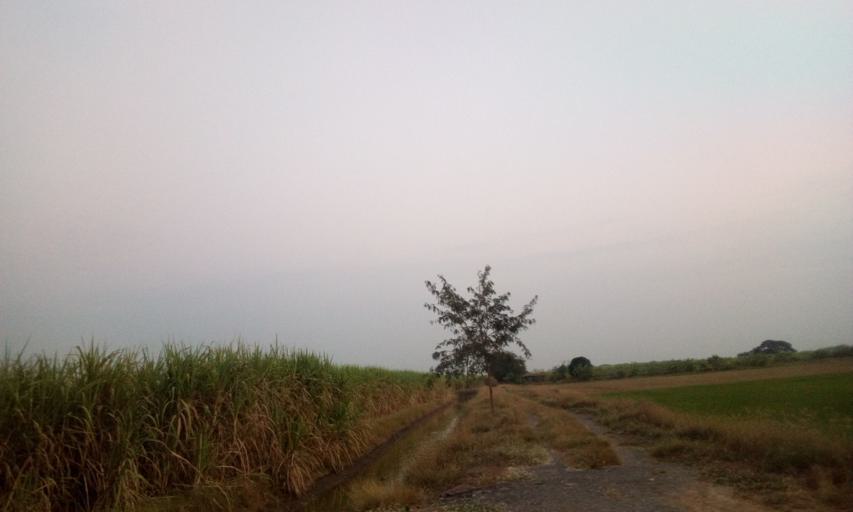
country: TH
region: Sing Buri
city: Phrom Buri
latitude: 14.8191
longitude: 100.4029
